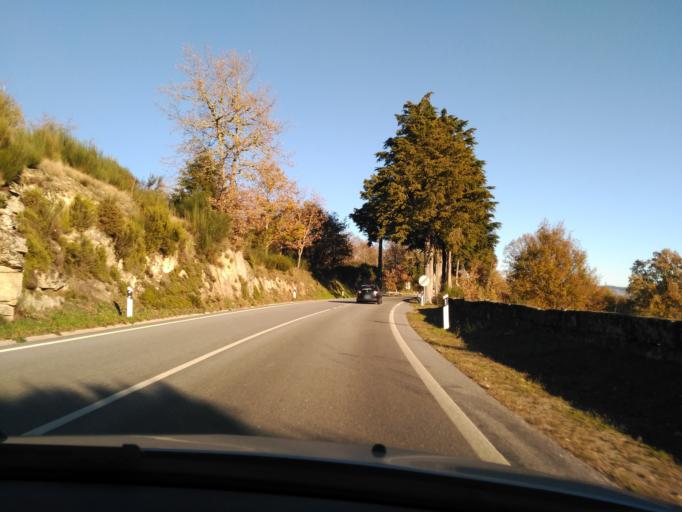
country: PT
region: Vila Real
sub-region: Montalegre
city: Montalegre
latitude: 41.7565
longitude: -7.8586
